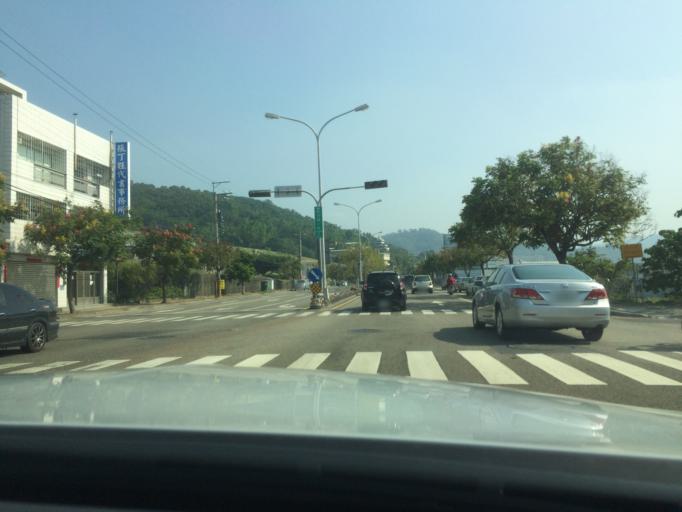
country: TW
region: Taiwan
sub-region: Taichung City
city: Taichung
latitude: 24.1812
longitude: 120.7240
